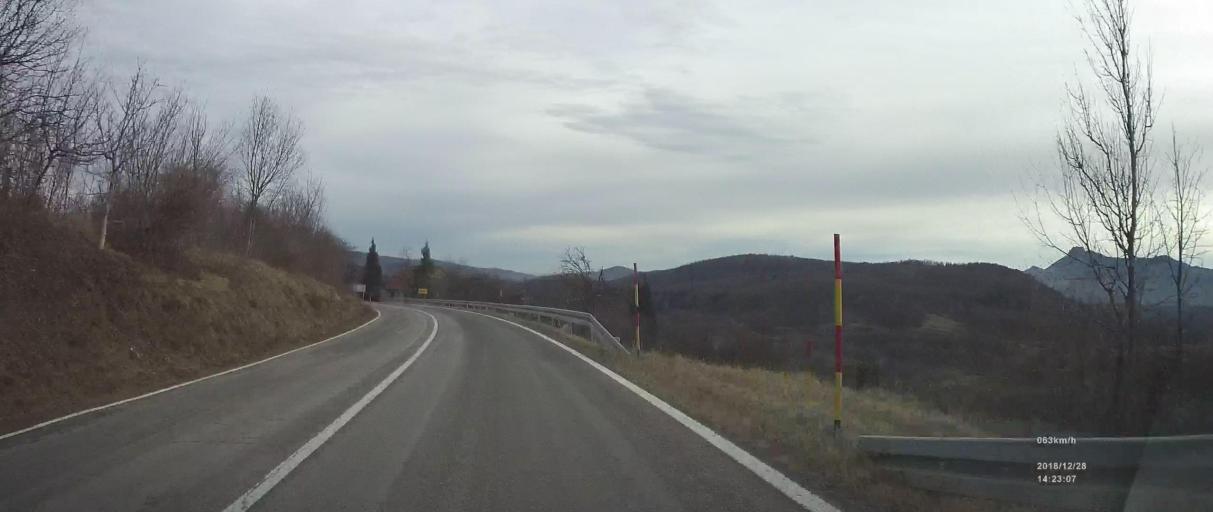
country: HR
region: Primorsko-Goranska
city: Vrbovsko
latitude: 45.3803
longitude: 15.0912
